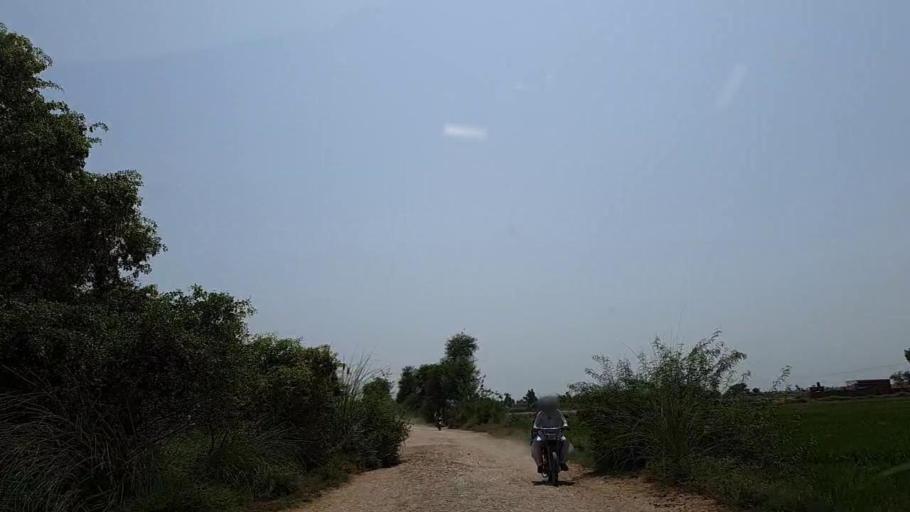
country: PK
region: Sindh
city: Adilpur
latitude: 27.9154
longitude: 69.3713
